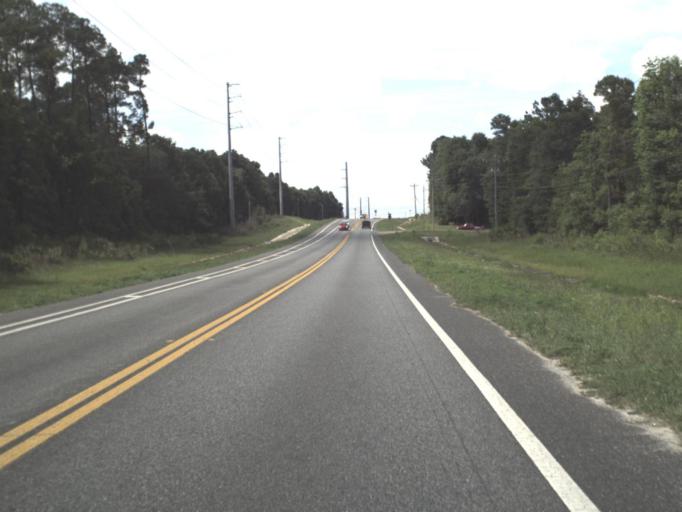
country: US
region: Florida
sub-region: Clay County
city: Middleburg
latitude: 30.0319
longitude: -81.8976
